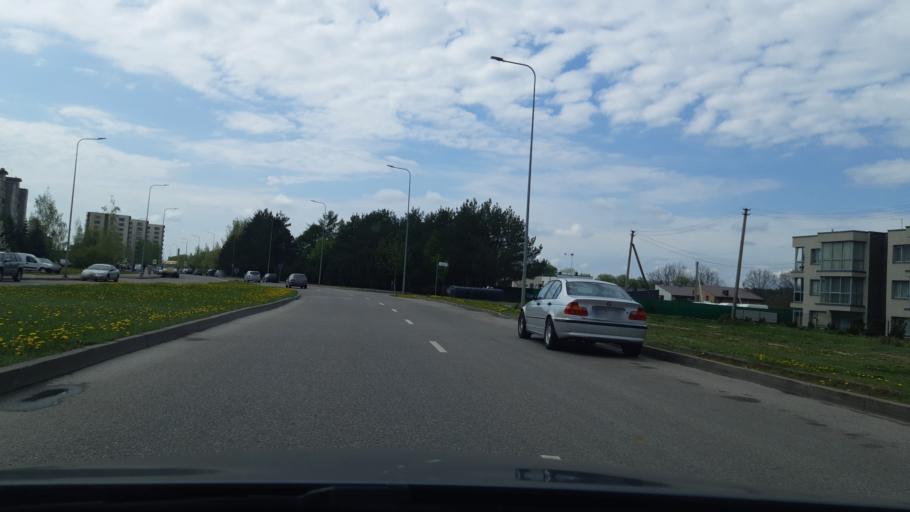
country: LT
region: Kauno apskritis
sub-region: Kaunas
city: Silainiai
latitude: 54.9211
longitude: 23.8669
